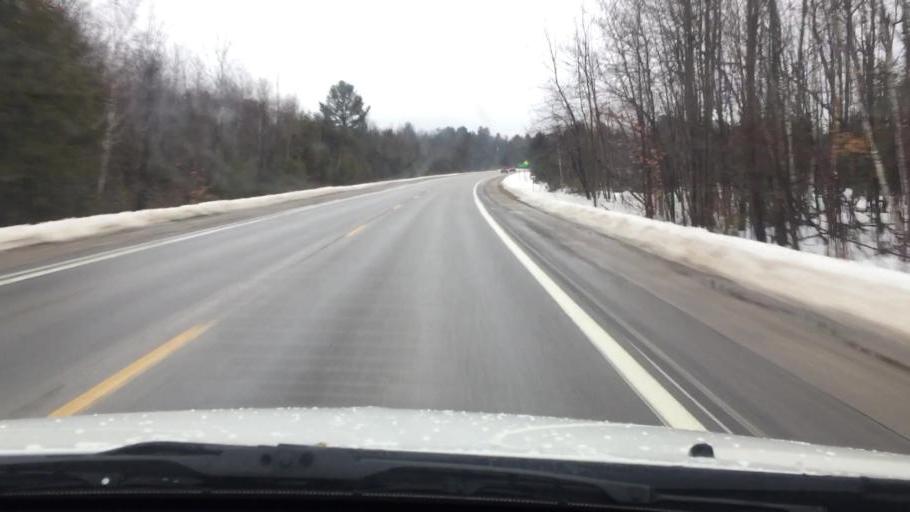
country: US
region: Michigan
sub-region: Charlevoix County
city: Charlevoix
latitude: 45.2620
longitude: -85.1942
